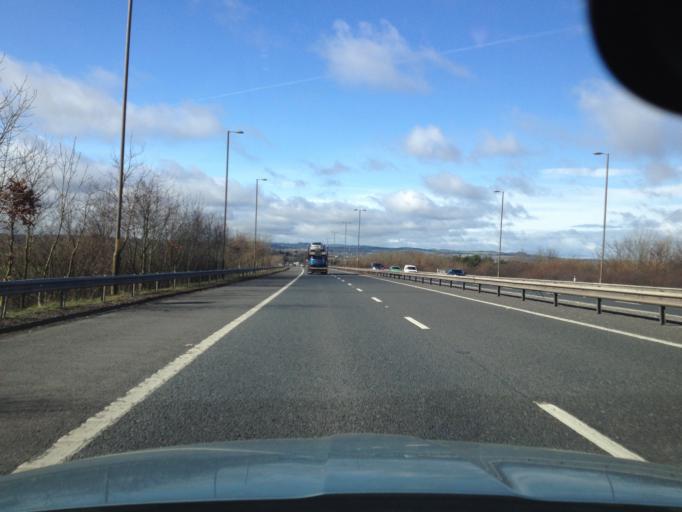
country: GB
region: Scotland
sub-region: Edinburgh
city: Newbridge
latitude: 55.9259
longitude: -3.4043
